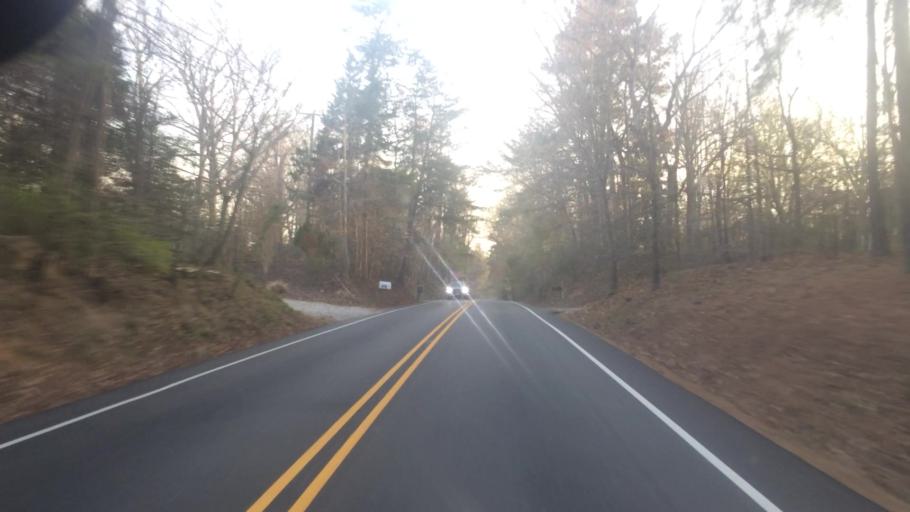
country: US
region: Virginia
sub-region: James City County
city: Williamsburg
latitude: 37.2419
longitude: -76.7435
